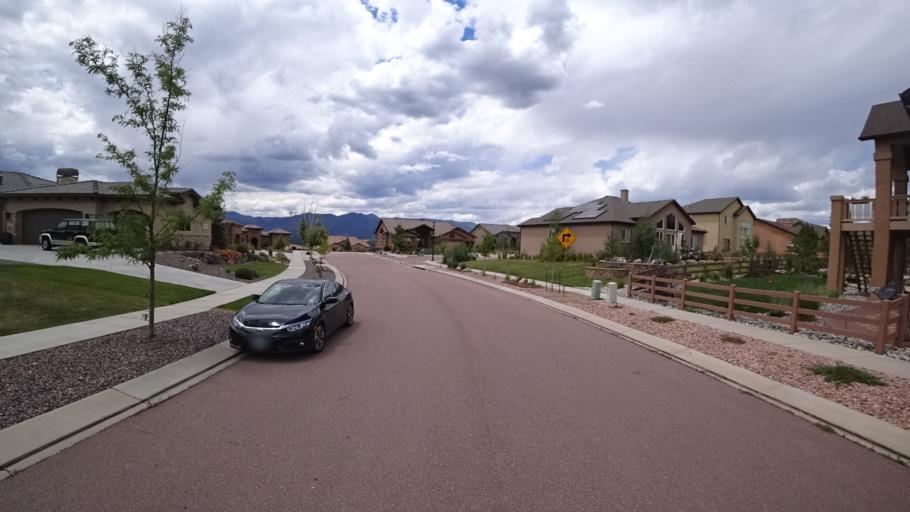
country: US
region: Colorado
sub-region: El Paso County
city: Gleneagle
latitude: 39.0209
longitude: -104.8018
